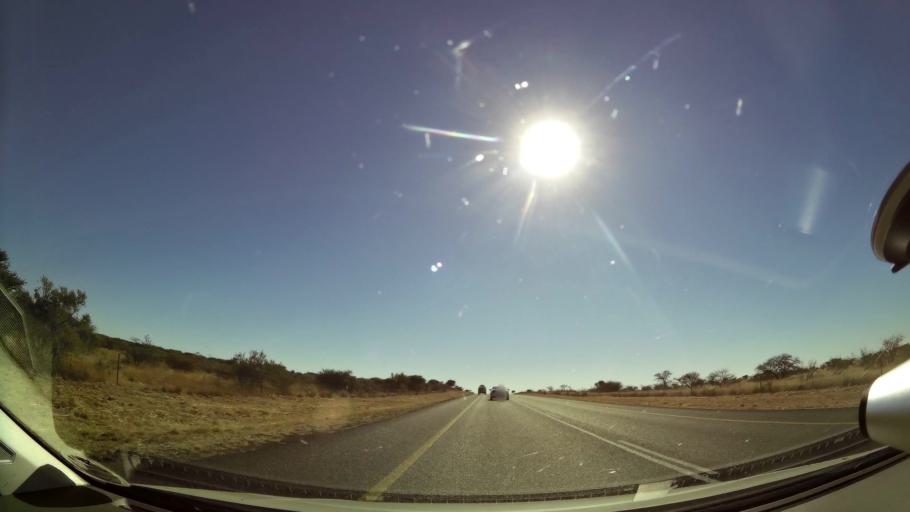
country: ZA
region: Northern Cape
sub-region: Frances Baard District Municipality
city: Warrenton
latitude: -28.3063
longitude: 24.8307
